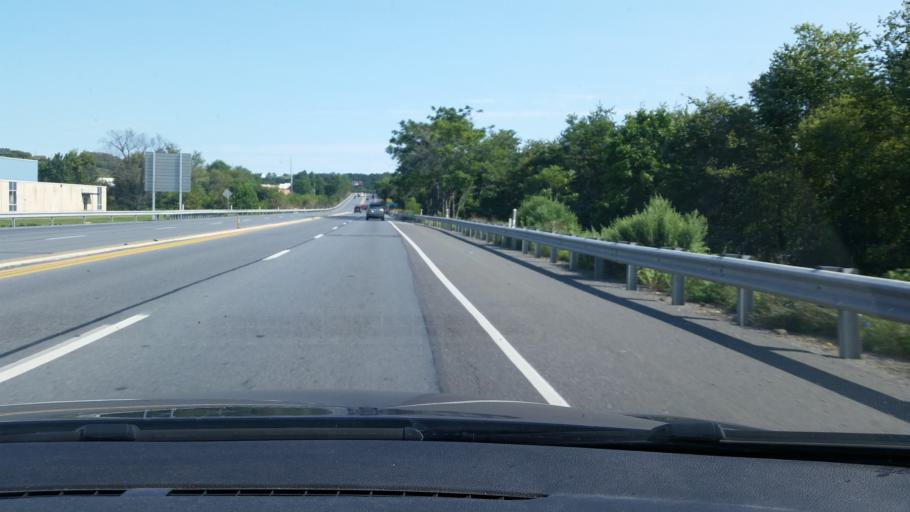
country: US
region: Pennsylvania
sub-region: Berks County
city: Hamburg
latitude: 40.5476
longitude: -75.9871
